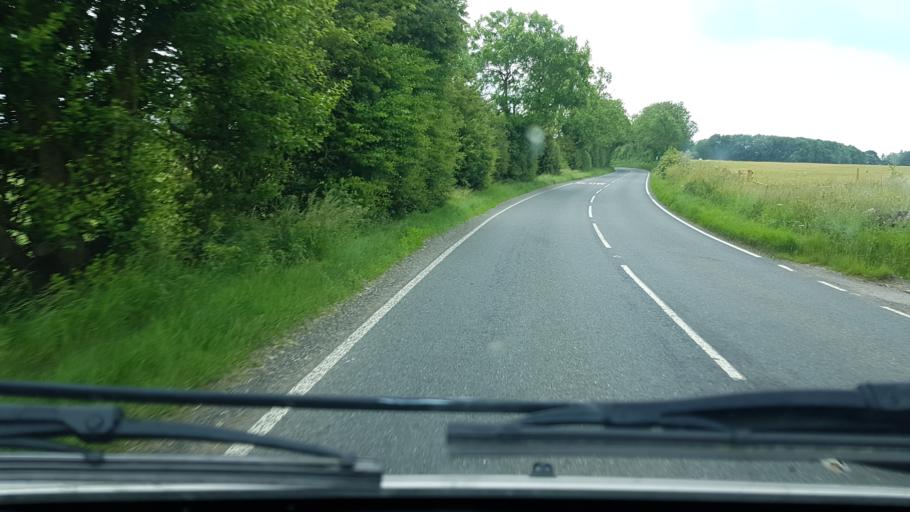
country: GB
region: England
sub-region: Gloucestershire
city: Donnington
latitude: 51.9444
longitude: -1.7310
